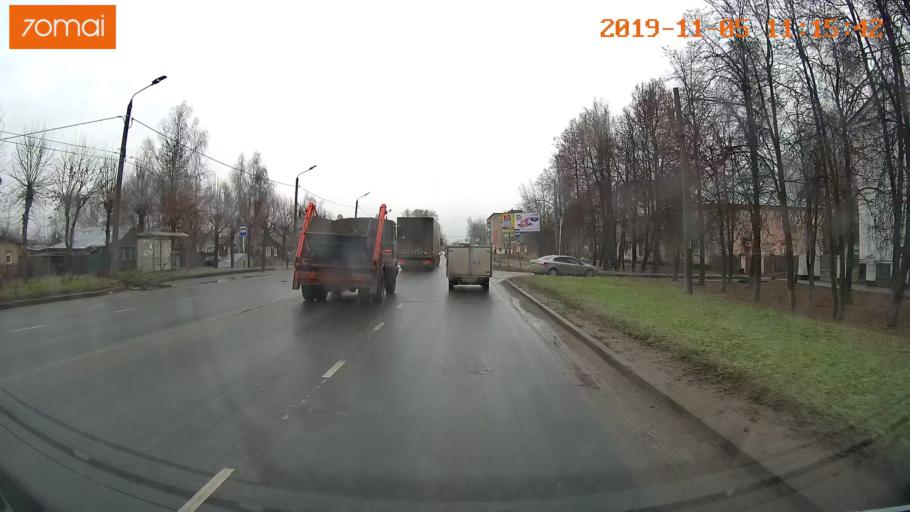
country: RU
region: Ivanovo
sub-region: Gorod Ivanovo
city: Ivanovo
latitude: 56.9791
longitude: 40.9540
